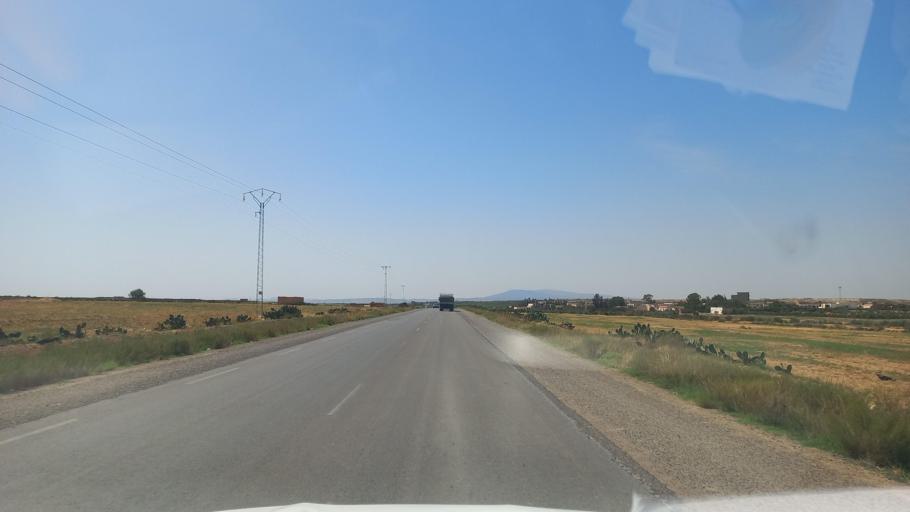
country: TN
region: Al Qasrayn
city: Sbiba
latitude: 35.3666
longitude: 9.0960
